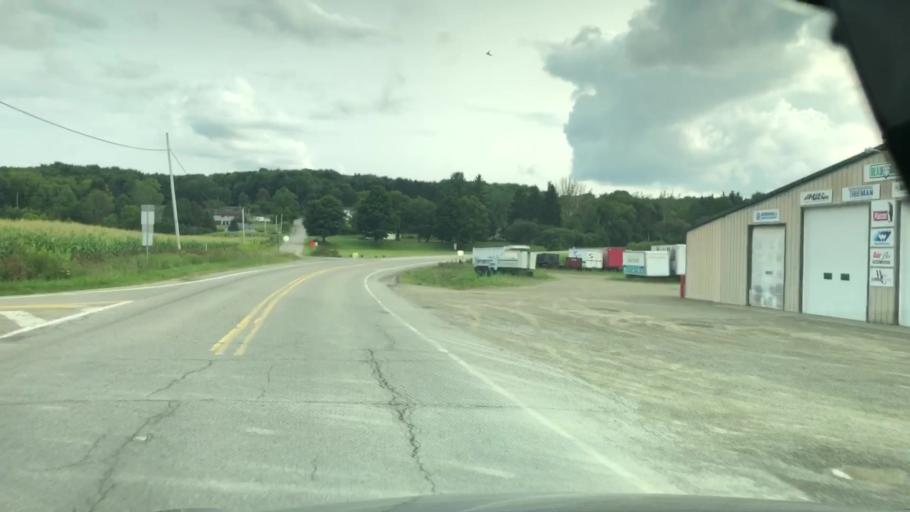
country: US
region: Pennsylvania
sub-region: Erie County
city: Union City
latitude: 41.9959
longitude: -79.8110
